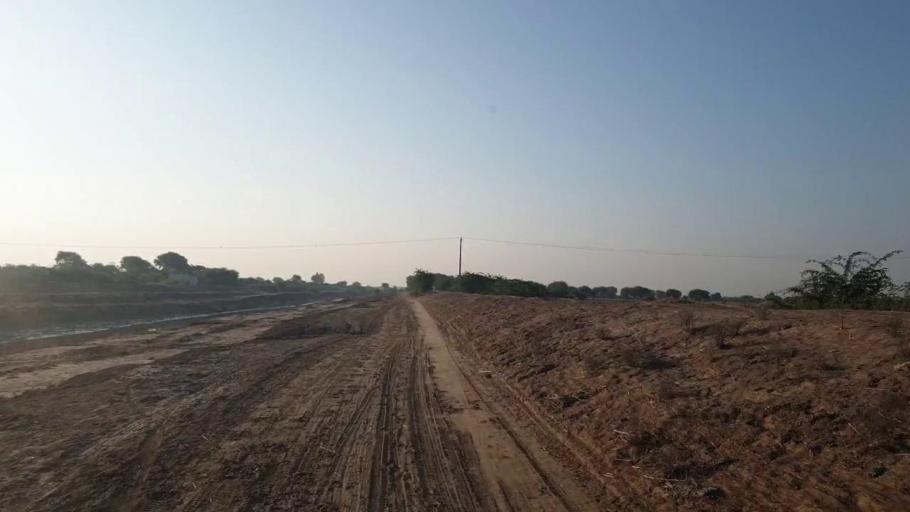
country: PK
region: Sindh
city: Badin
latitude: 24.6485
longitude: 68.7897
